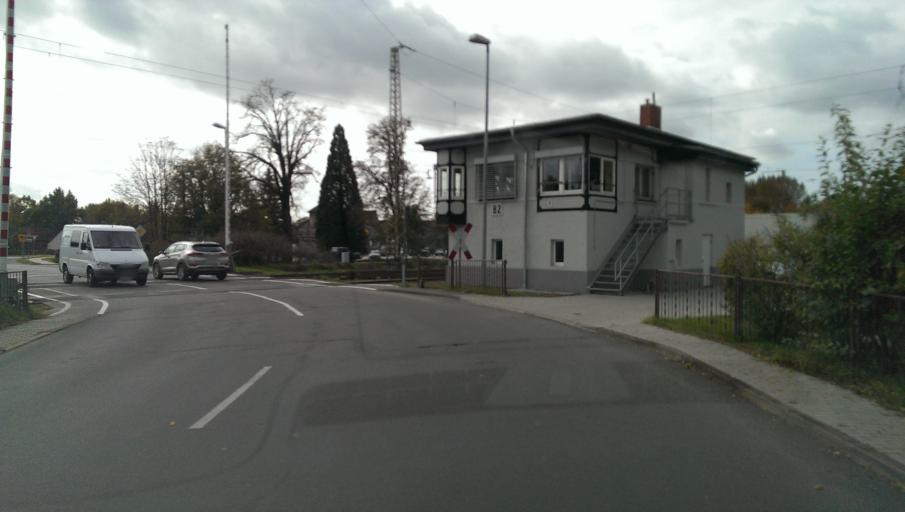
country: DE
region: Brandenburg
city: Doberlug-Kirchhain
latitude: 51.6203
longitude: 13.5610
